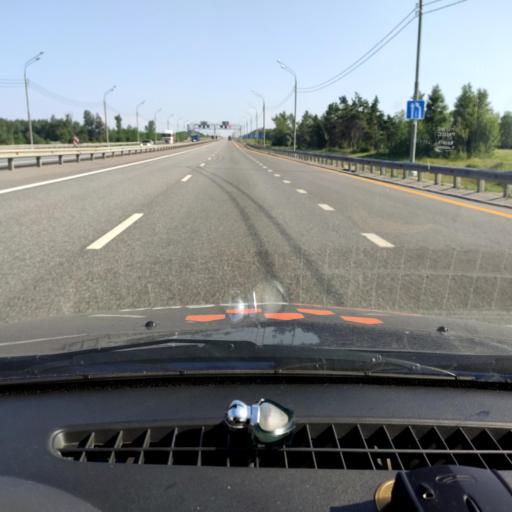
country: RU
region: Lipetsk
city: Khlevnoye
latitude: 52.2847
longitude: 39.0518
